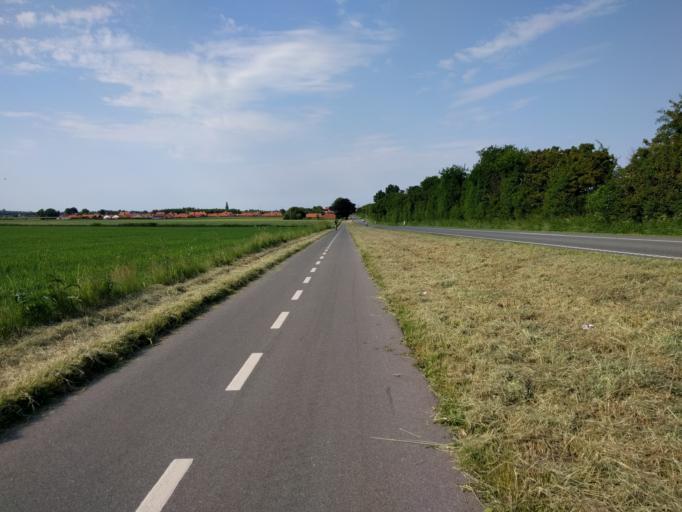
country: DK
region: South Denmark
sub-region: Kerteminde Kommune
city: Kerteminde
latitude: 55.4328
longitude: 10.6542
